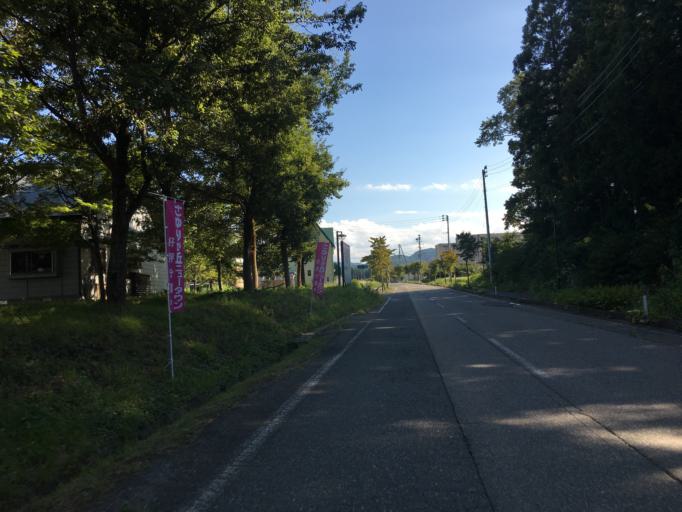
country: JP
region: Fukushima
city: Kitakata
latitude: 37.6023
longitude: 139.6521
